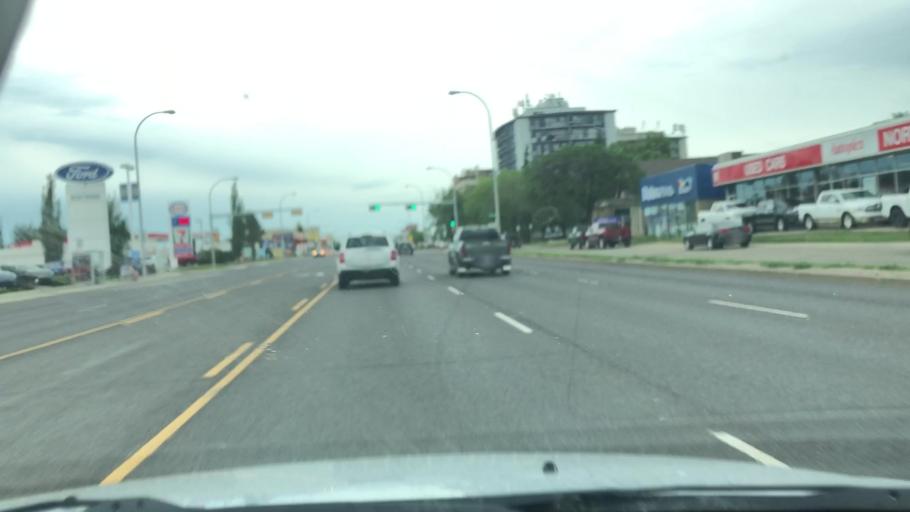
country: CA
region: Alberta
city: Edmonton
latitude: 53.5938
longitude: -113.4920
